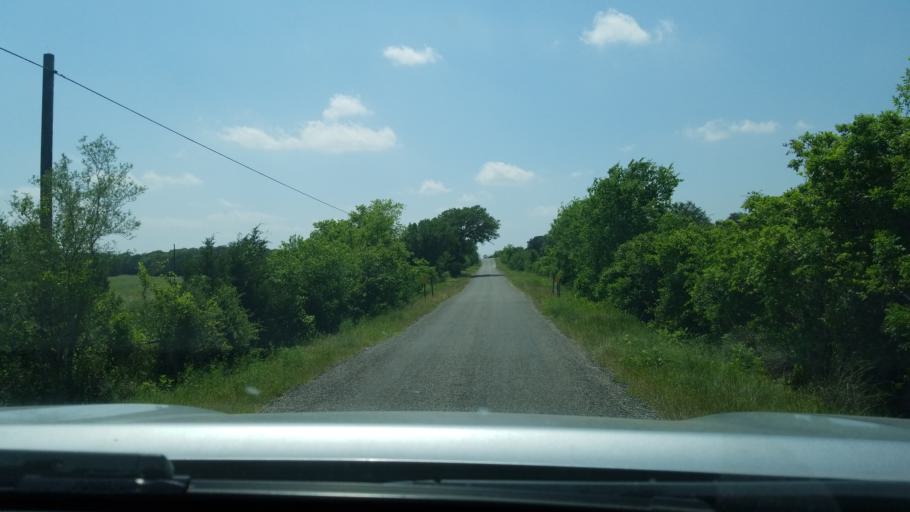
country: US
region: Texas
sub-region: Blanco County
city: Blanco
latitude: 29.9906
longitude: -98.5290
